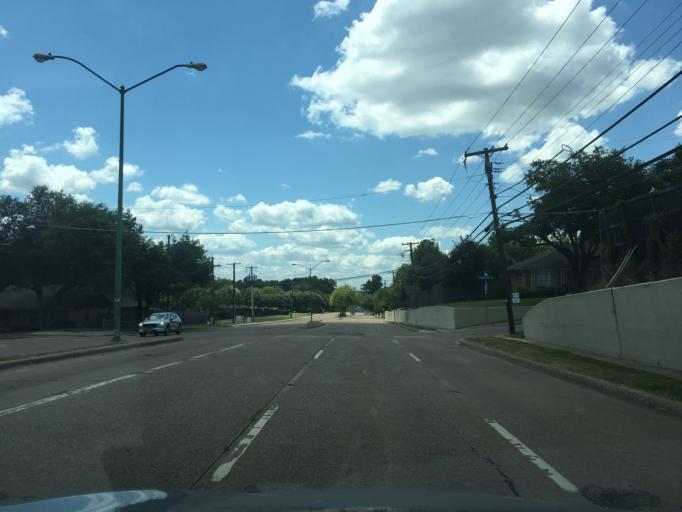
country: US
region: Texas
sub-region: Dallas County
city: Richardson
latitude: 32.8734
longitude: -96.7180
